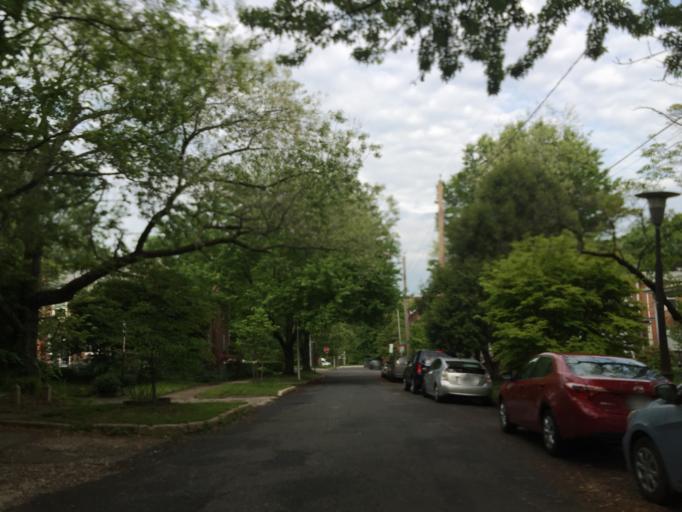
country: US
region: Maryland
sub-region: City of Baltimore
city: Baltimore
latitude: 39.3353
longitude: -76.6280
